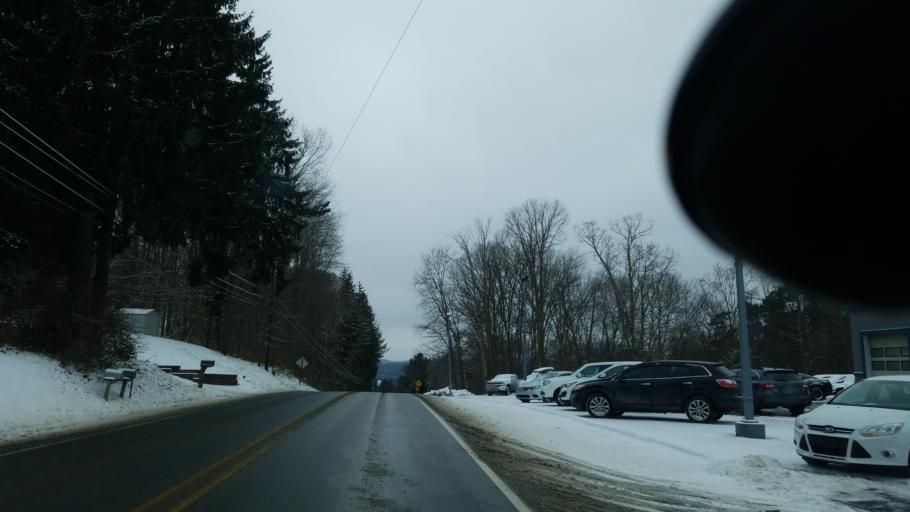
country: US
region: Pennsylvania
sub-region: Jefferson County
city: Albion
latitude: 40.9395
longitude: -78.9471
